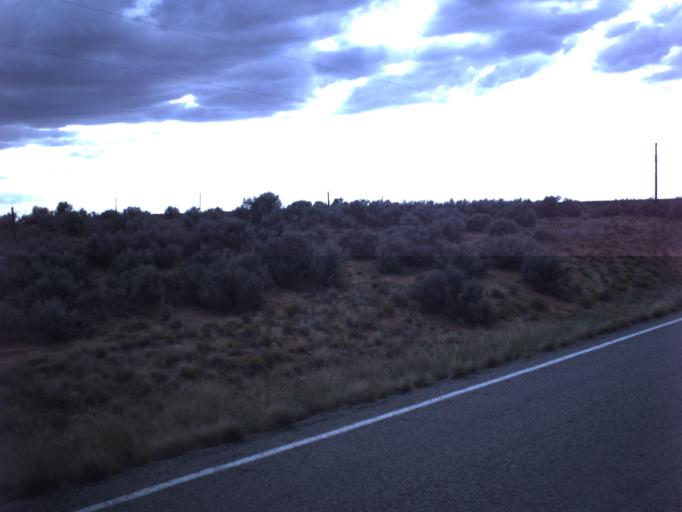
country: US
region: Utah
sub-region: San Juan County
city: Blanding
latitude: 37.4265
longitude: -109.3510
